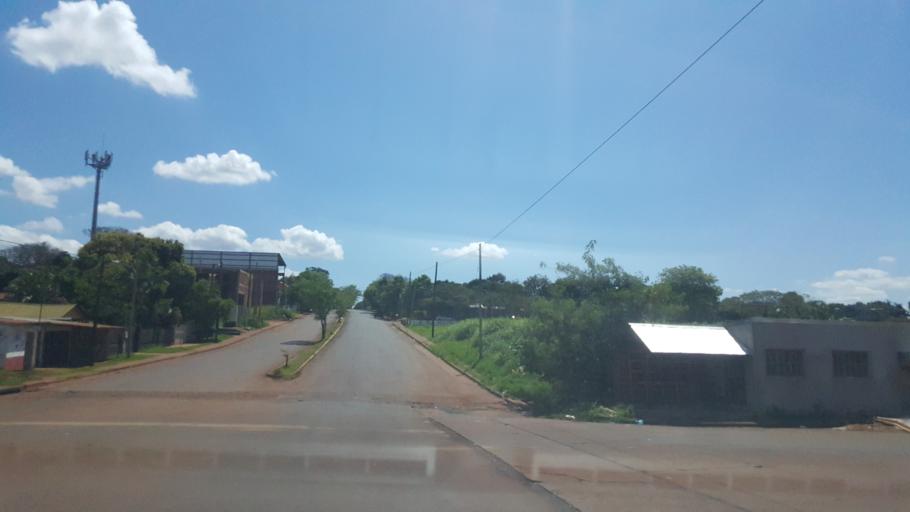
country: AR
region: Misiones
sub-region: Departamento de Capital
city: Posadas
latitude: -27.3806
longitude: -55.9333
